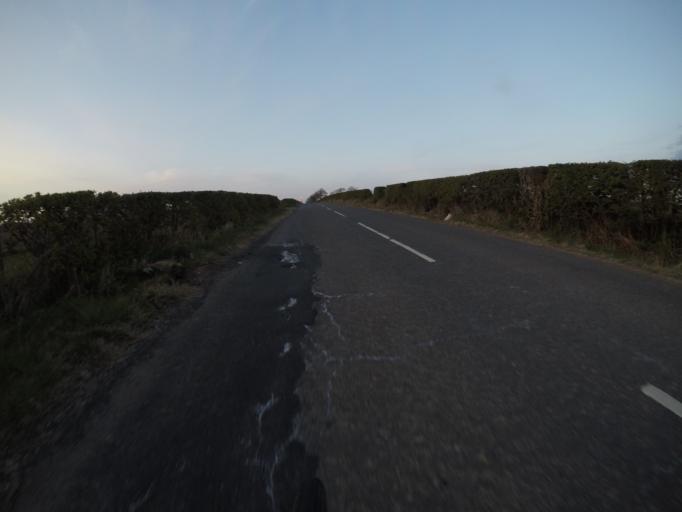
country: GB
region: Scotland
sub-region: South Ayrshire
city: Dundonald
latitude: 55.5598
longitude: -4.6098
